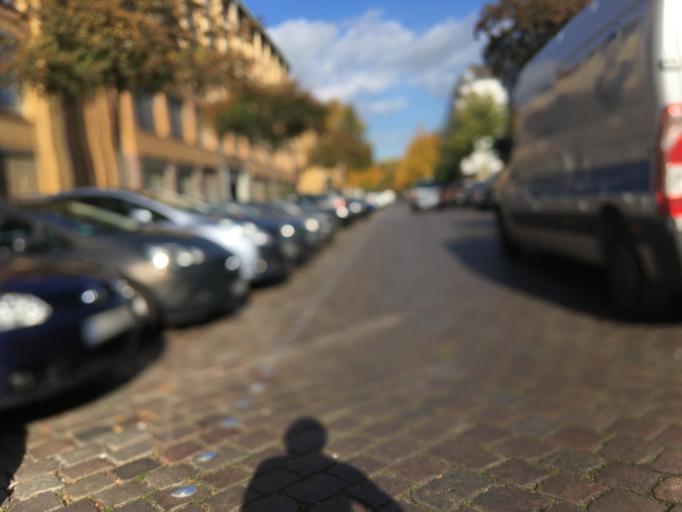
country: DE
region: Berlin
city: Wedding Bezirk
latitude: 52.5527
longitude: 13.3620
